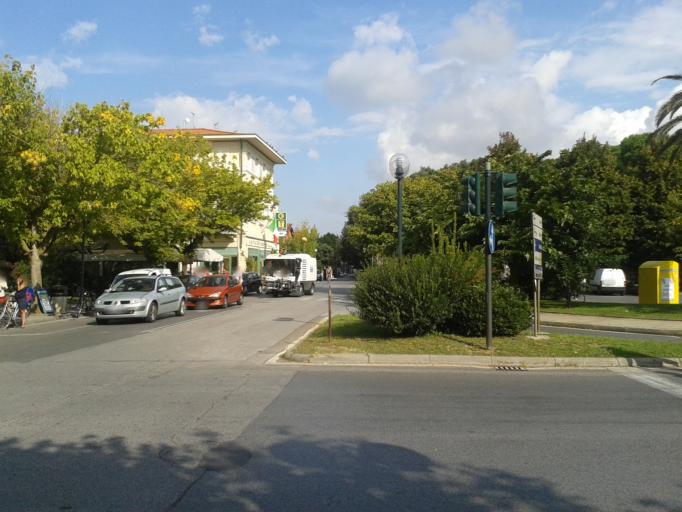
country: IT
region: Tuscany
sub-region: Provincia di Lucca
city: Pietrasanta
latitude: 43.9375
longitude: 10.1913
